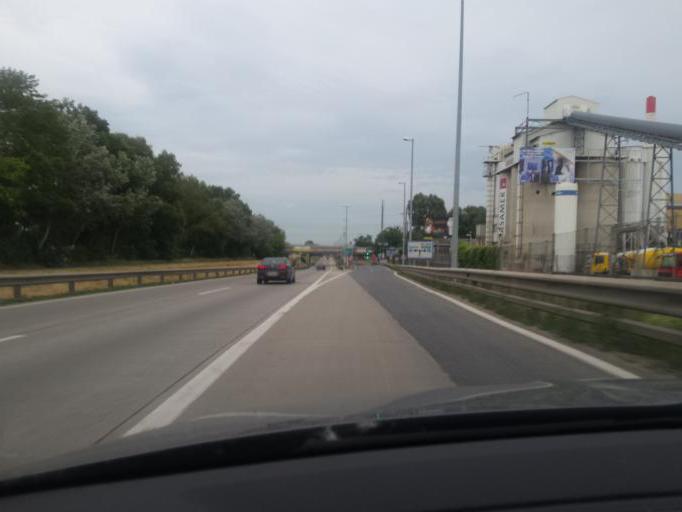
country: AT
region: Vienna
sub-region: Wien Stadt
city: Vienna
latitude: 48.1869
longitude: 16.4277
